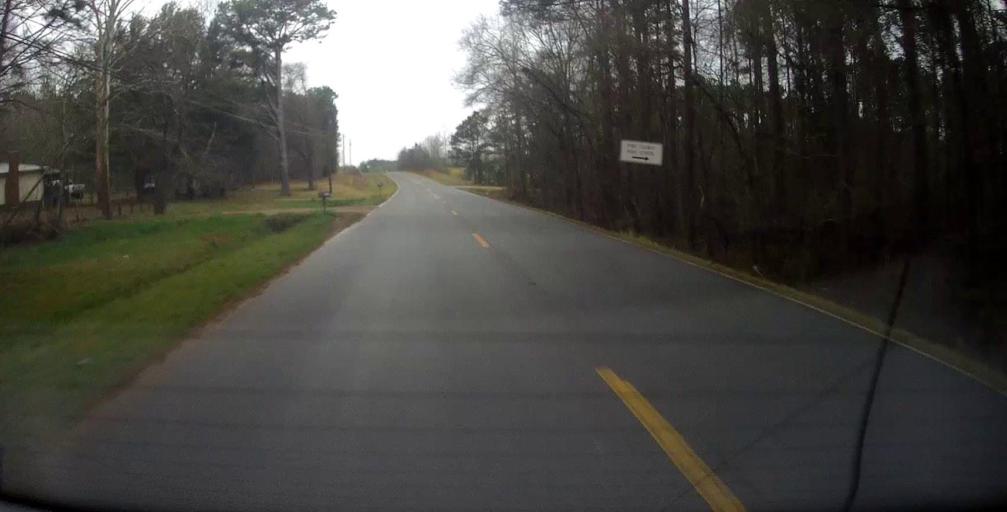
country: US
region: Georgia
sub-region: Pike County
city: Zebulon
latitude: 33.0868
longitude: -84.3344
